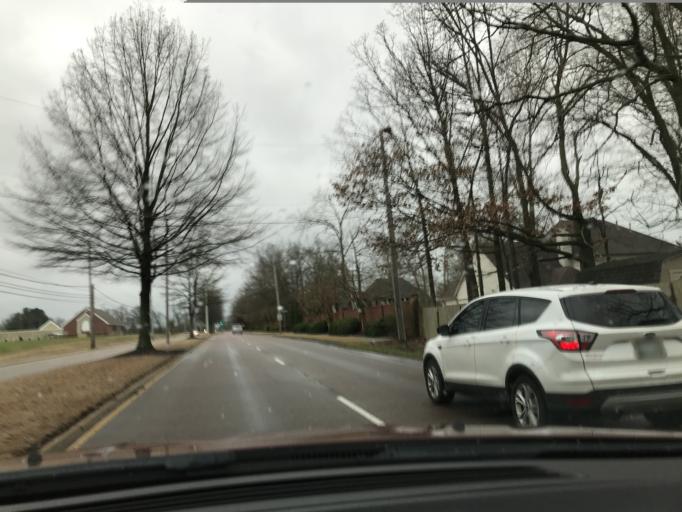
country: US
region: Tennessee
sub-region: Shelby County
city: Collierville
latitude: 35.0576
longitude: -89.6861
